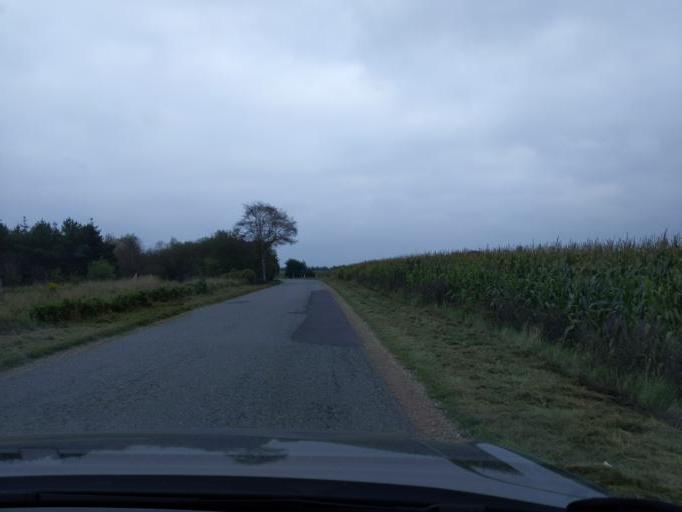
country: DK
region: Central Jutland
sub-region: Viborg Kommune
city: Karup
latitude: 56.3696
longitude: 9.2576
